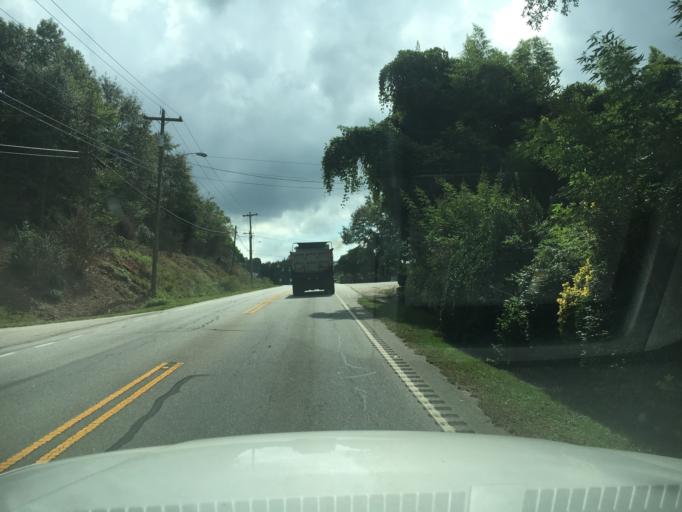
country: US
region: South Carolina
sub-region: Greenville County
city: Greer
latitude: 34.9576
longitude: -82.2302
